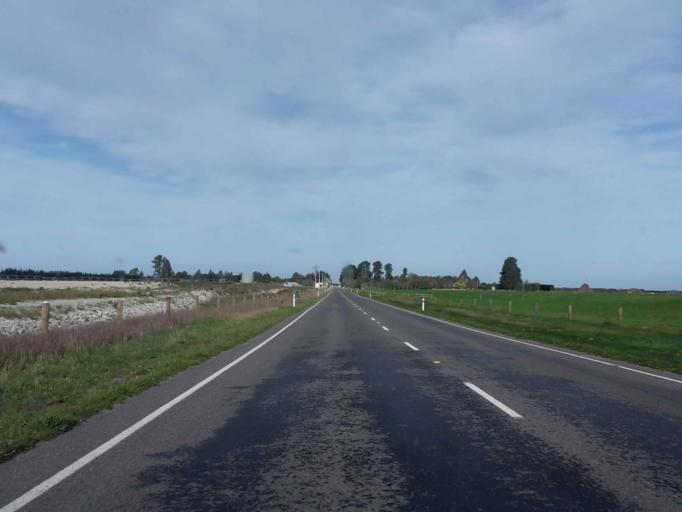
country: NZ
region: Canterbury
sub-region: Timaru District
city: Pleasant Point
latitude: -44.0587
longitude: 171.3503
